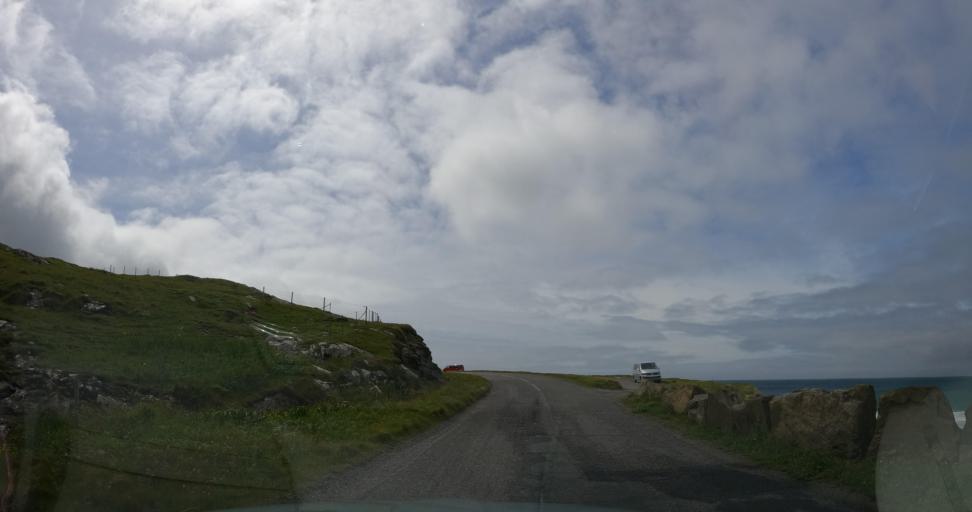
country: GB
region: Scotland
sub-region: Eilean Siar
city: Barra
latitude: 56.9919
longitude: -7.5078
